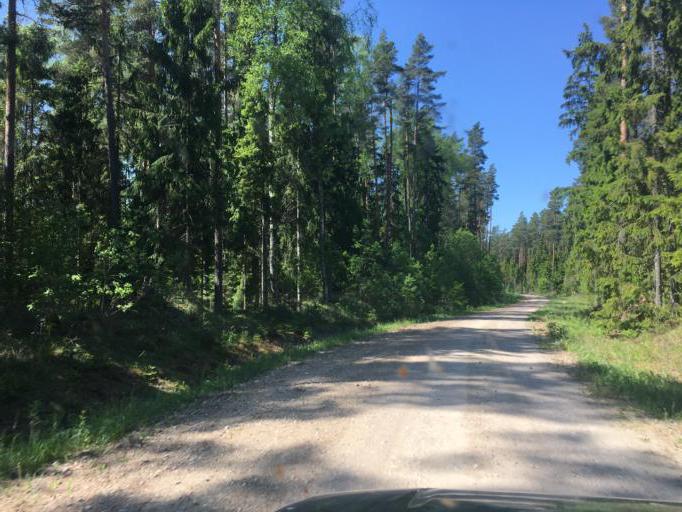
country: LV
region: Talsu Rajons
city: Valdemarpils
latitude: 57.4387
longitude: 22.6763
